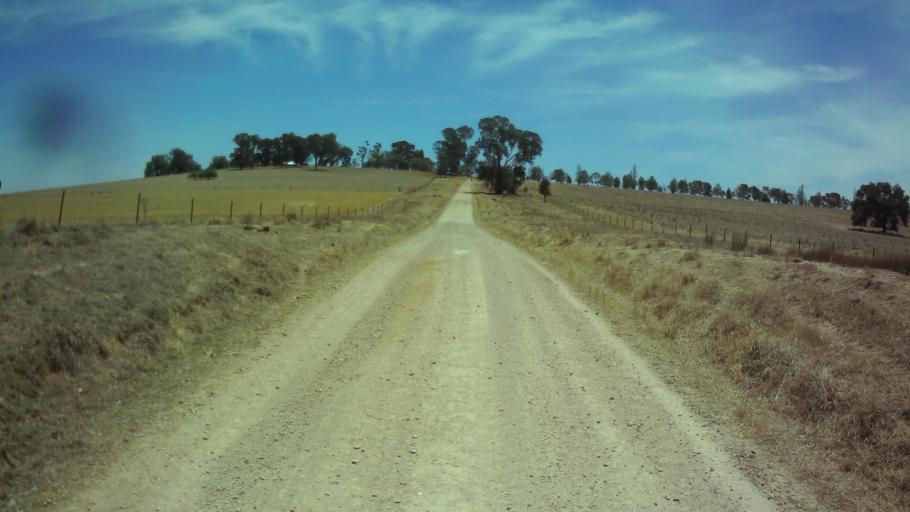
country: AU
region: New South Wales
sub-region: Weddin
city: Grenfell
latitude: -34.0202
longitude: 148.4289
